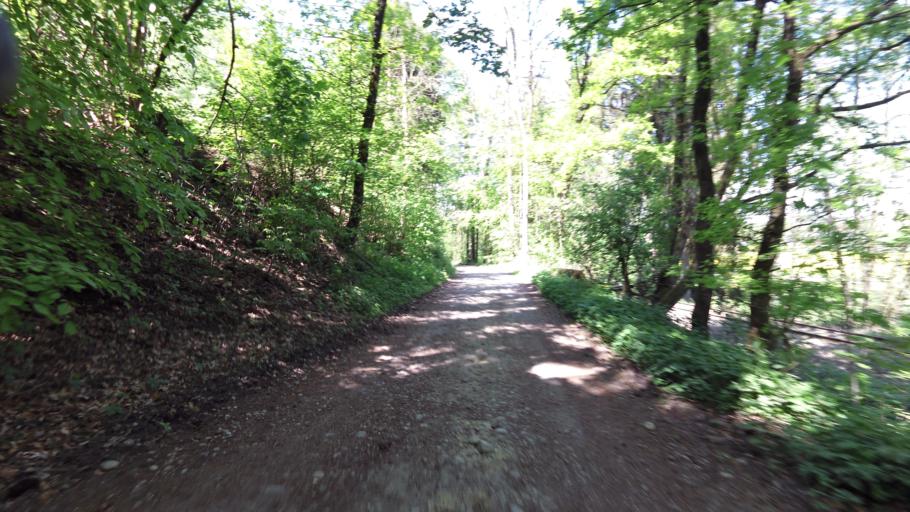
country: DE
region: Bavaria
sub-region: Lower Bavaria
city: Weihmichl
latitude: 48.5670
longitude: 12.0803
